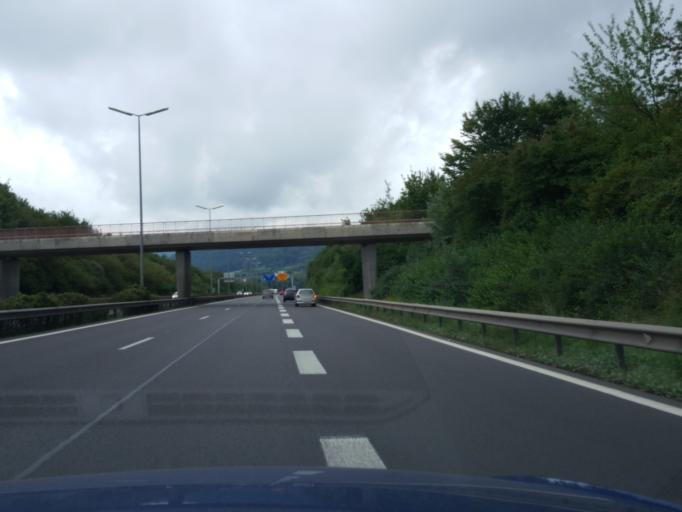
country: LU
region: Luxembourg
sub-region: Canton de Mersch
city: Mersch
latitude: 49.7587
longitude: 6.0917
